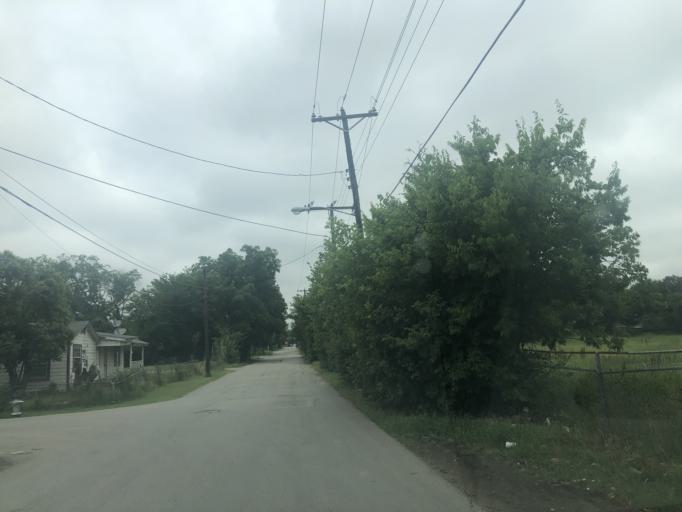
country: US
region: Texas
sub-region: Dallas County
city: Dallas
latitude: 32.7748
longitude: -96.8479
